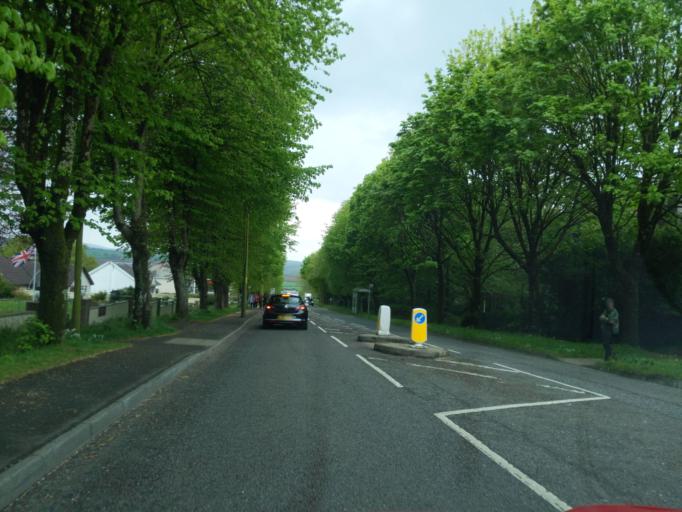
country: GB
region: England
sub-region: Cornwall
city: Bodmin
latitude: 50.4672
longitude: -4.7390
